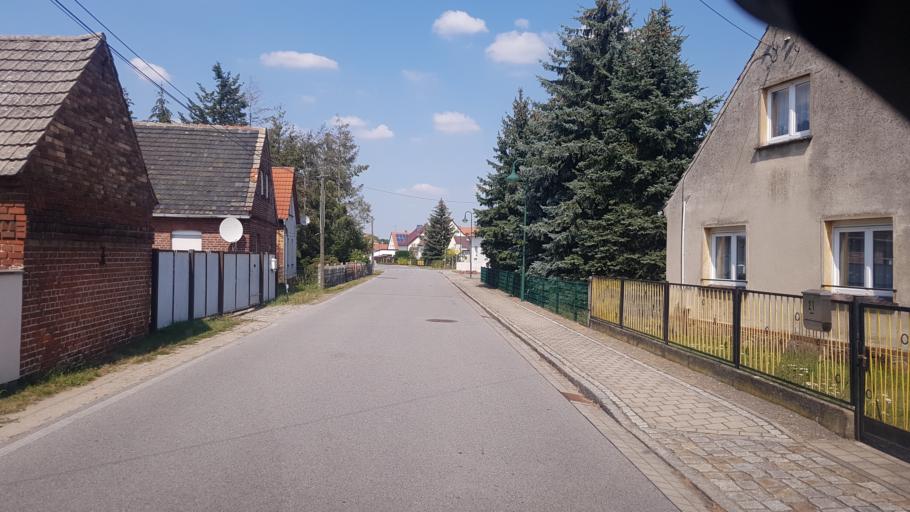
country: DE
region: Brandenburg
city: Cottbus
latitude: 51.6961
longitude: 14.4259
